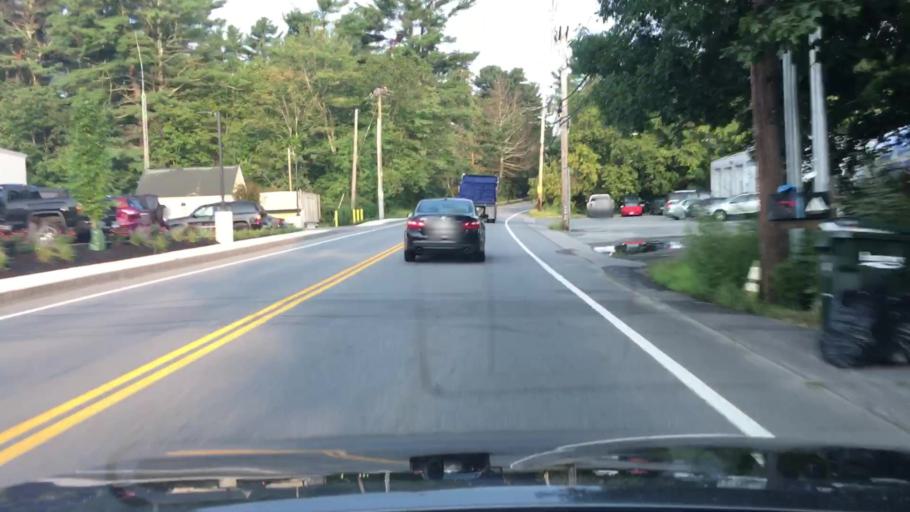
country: US
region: Massachusetts
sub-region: Middlesex County
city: Hopkinton
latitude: 42.2282
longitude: -71.5422
